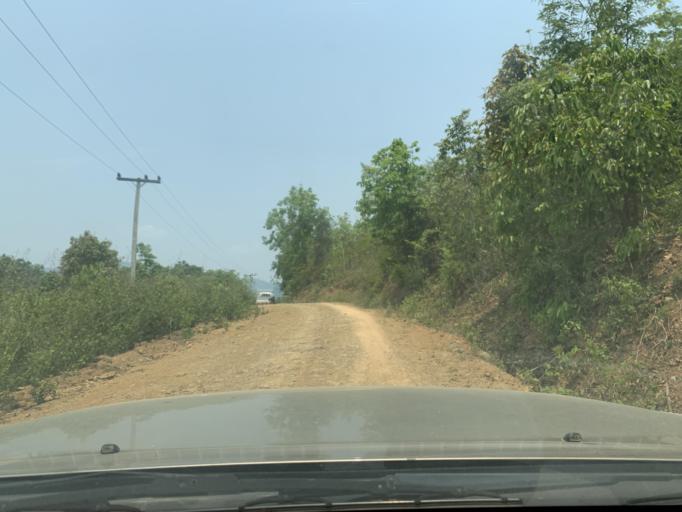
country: LA
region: Louangphabang
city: Louangphabang
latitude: 19.9537
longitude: 102.1282
